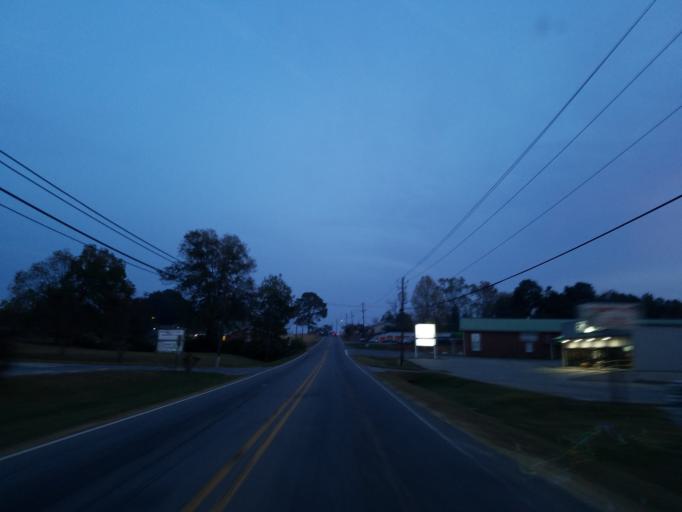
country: US
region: Georgia
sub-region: Pickens County
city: Jasper
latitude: 34.4730
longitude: -84.4374
